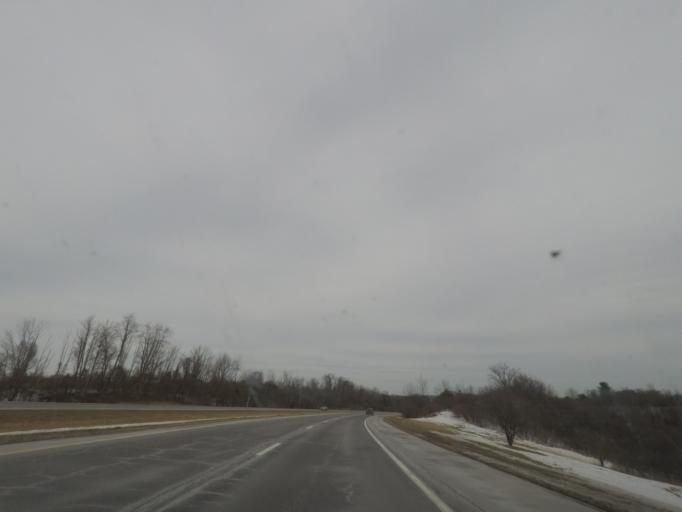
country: US
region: New York
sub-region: Albany County
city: Delmar
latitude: 42.6161
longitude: -73.8014
